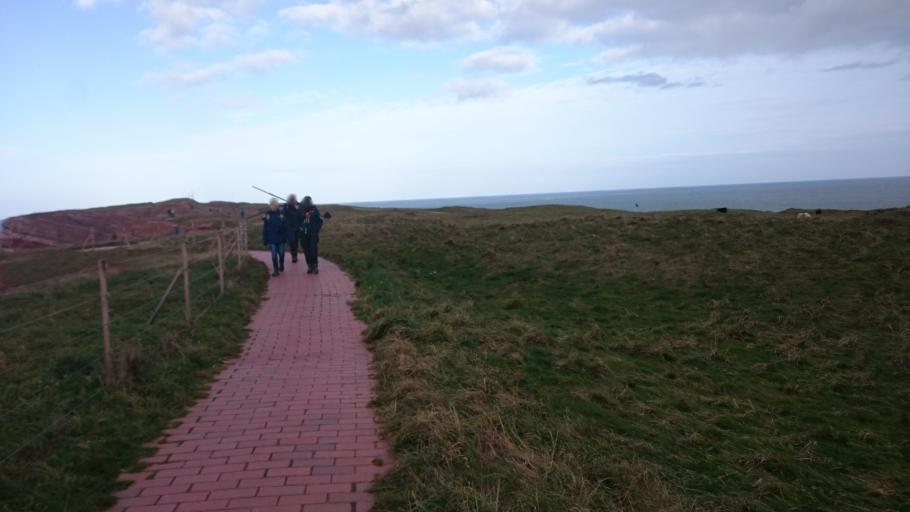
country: DE
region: Schleswig-Holstein
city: Helgoland
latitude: 54.1829
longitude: 7.8798
